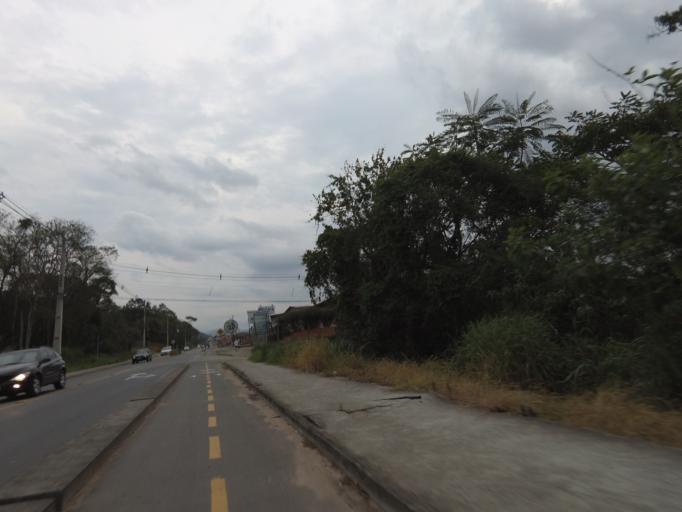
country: BR
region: Santa Catarina
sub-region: Blumenau
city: Blumenau
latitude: -26.8849
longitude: -49.0628
